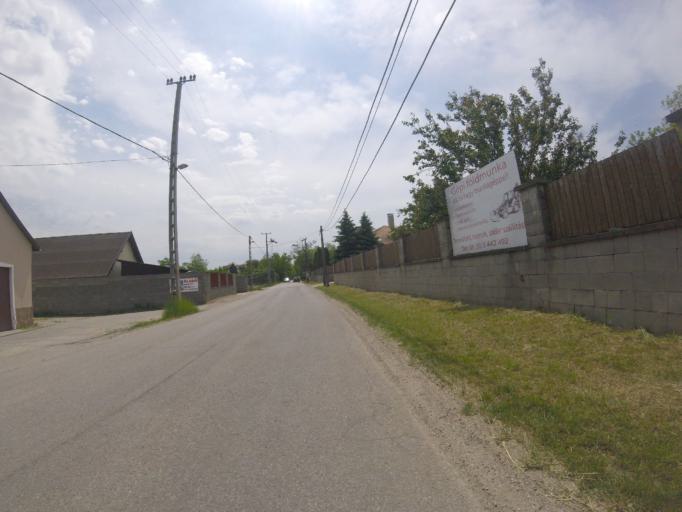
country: HU
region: Pest
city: Tahitotfalu
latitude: 47.7472
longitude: 19.0964
